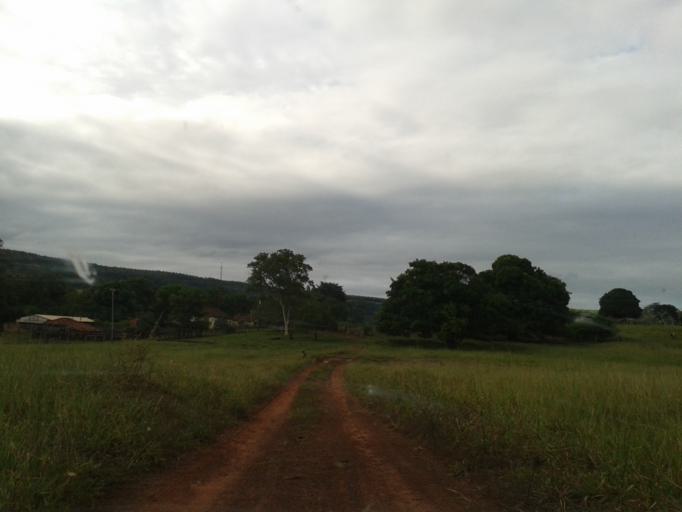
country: BR
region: Minas Gerais
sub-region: Campina Verde
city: Campina Verde
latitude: -19.4718
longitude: -49.6360
